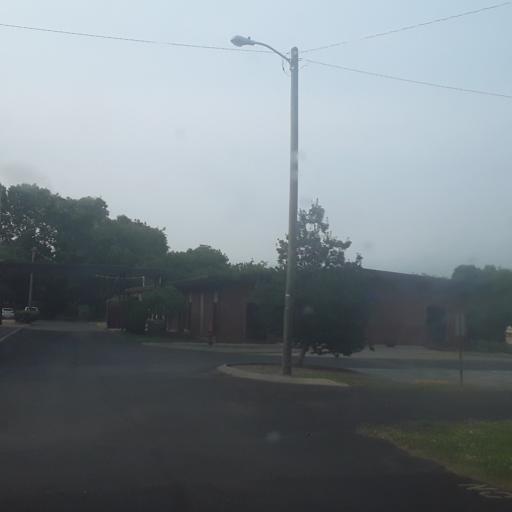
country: US
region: Tennessee
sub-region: Davidson County
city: Oak Hill
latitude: 36.0760
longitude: -86.7574
